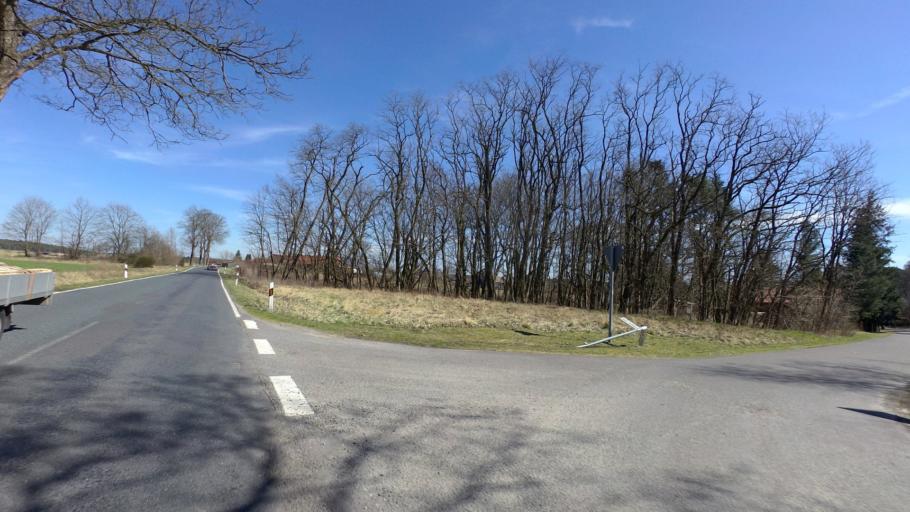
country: DE
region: Brandenburg
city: Munchehofe
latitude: 52.1598
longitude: 13.8689
